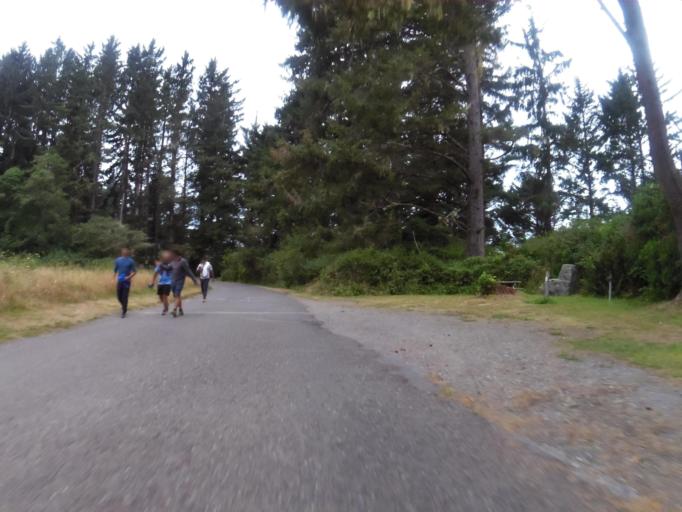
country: US
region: California
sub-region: Humboldt County
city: Westhaven-Moonstone
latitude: 41.1406
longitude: -124.1592
